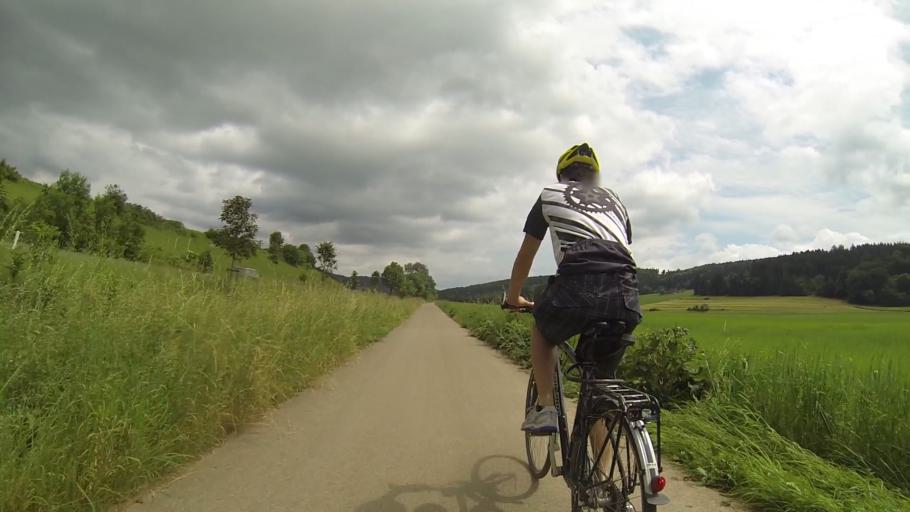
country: DE
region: Baden-Wuerttemberg
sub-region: Regierungsbezirk Stuttgart
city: Steinheim am Albuch
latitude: 48.6739
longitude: 10.0728
